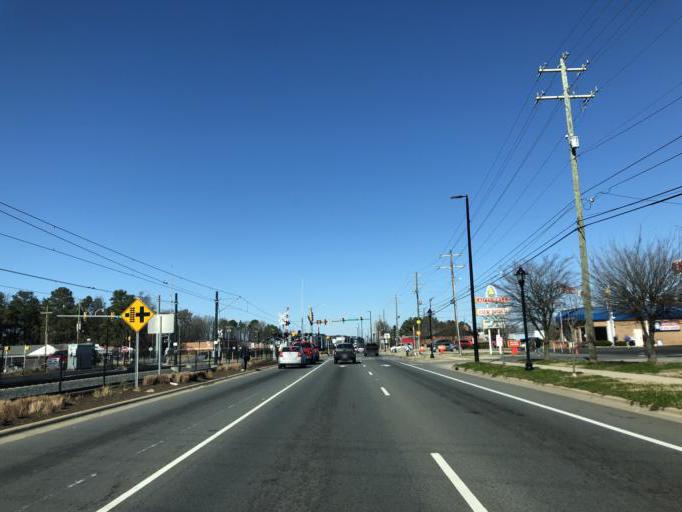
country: US
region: North Carolina
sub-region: Mecklenburg County
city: Charlotte
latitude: 35.2765
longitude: -80.7664
